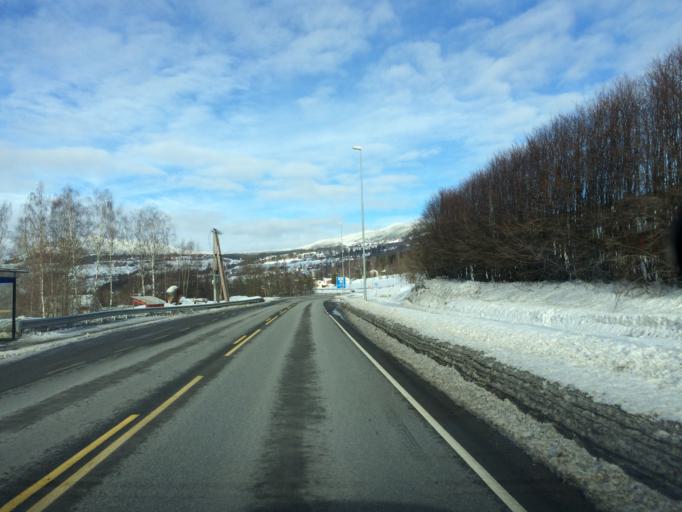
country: NO
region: Oppland
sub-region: Gausdal
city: Segalstad bru
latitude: 61.2071
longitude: 10.2990
